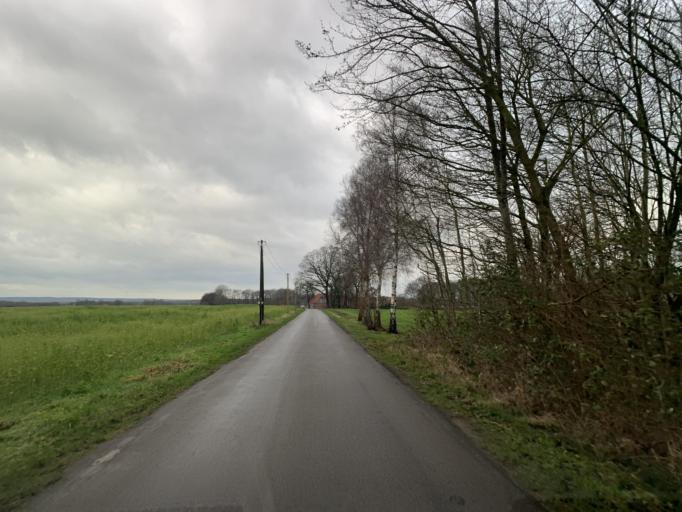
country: DE
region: North Rhine-Westphalia
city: Olfen
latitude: 51.7706
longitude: 7.3724
